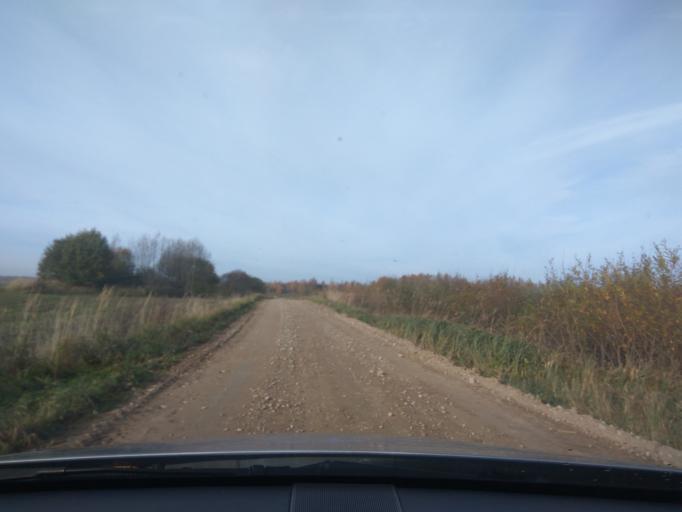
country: LV
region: Aizpute
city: Aizpute
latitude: 56.8444
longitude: 21.7080
